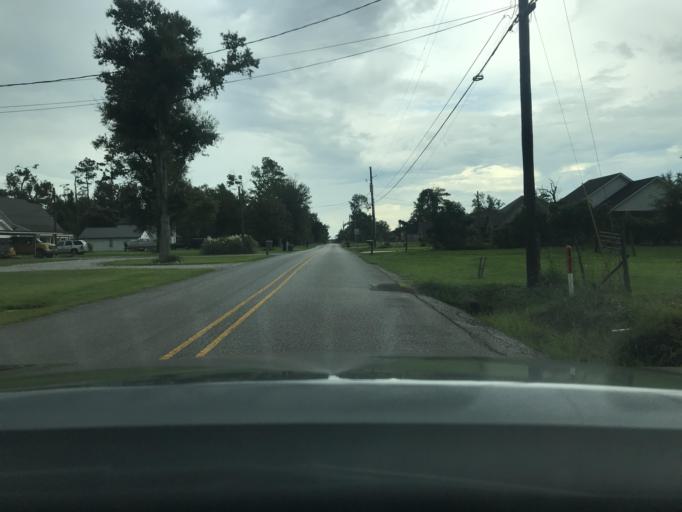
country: US
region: Louisiana
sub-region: Calcasieu Parish
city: Westlake
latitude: 30.2570
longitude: -93.2385
